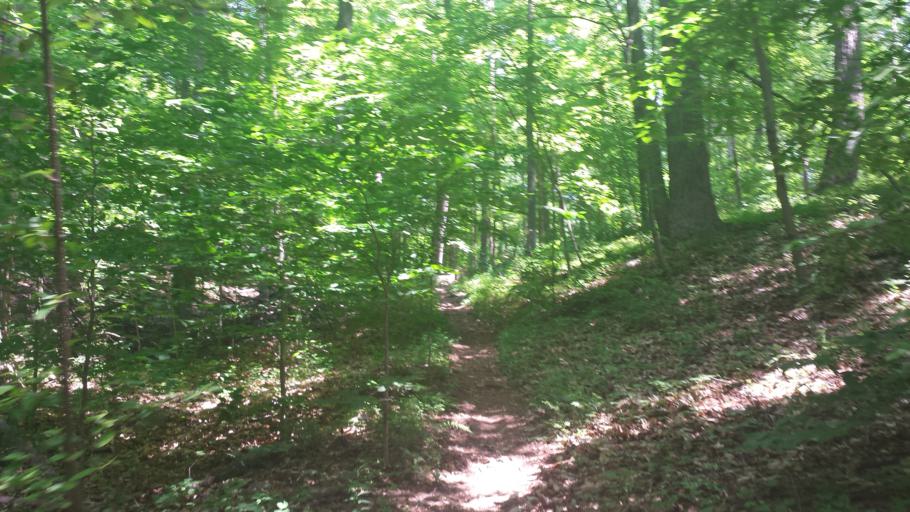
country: US
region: New York
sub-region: Westchester County
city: Valhalla
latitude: 41.0773
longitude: -73.7546
